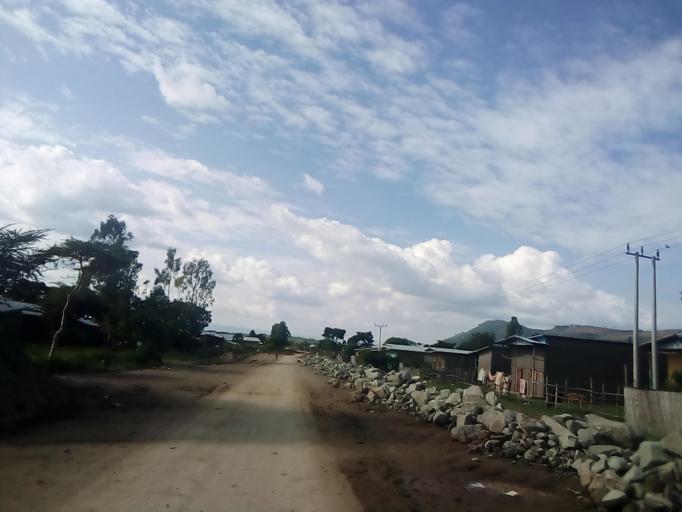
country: ET
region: Southern Nations, Nationalities, and People's Region
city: K'olito
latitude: 7.6052
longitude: 38.0663
